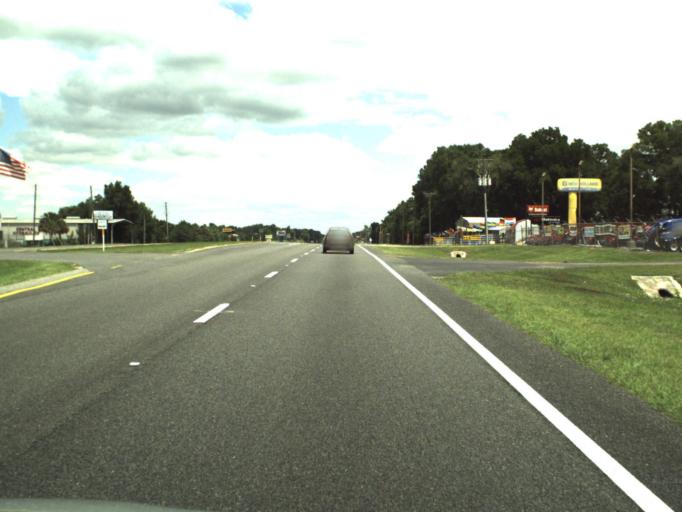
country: US
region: Florida
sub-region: Marion County
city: Ocala
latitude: 29.2464
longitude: -82.1520
